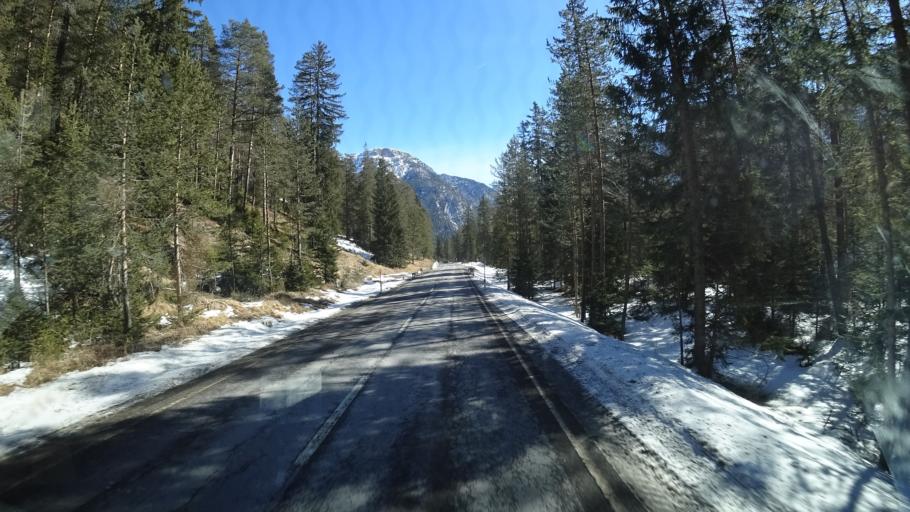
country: IT
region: Veneto
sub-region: Provincia di Belluno
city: Cortina d'Ampezzo
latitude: 46.6228
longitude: 12.2011
